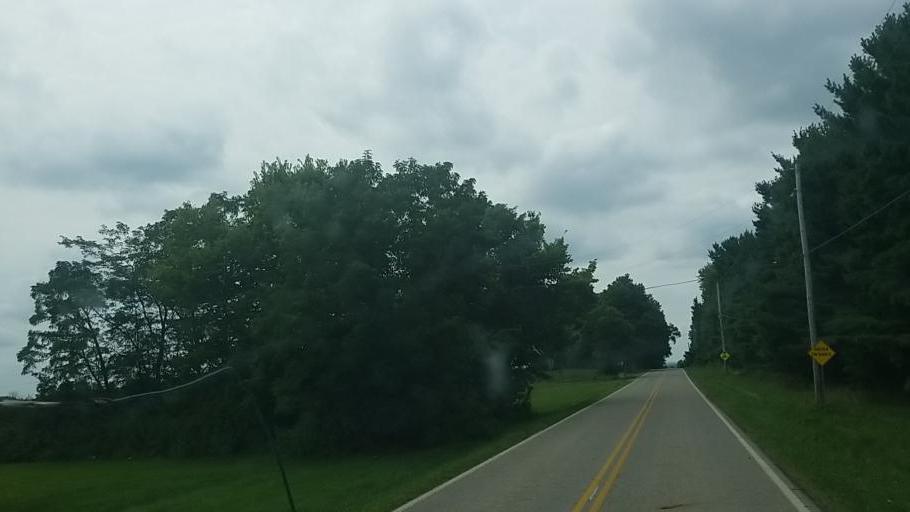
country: US
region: Ohio
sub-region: Fairfield County
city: Lithopolis
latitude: 39.7528
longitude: -82.8607
